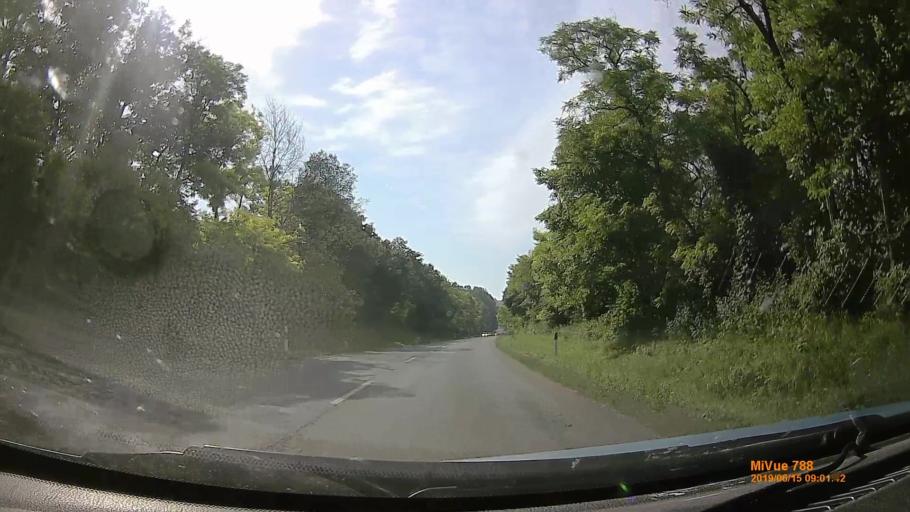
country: HU
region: Tolna
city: Iregszemcse
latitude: 46.7634
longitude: 18.1533
